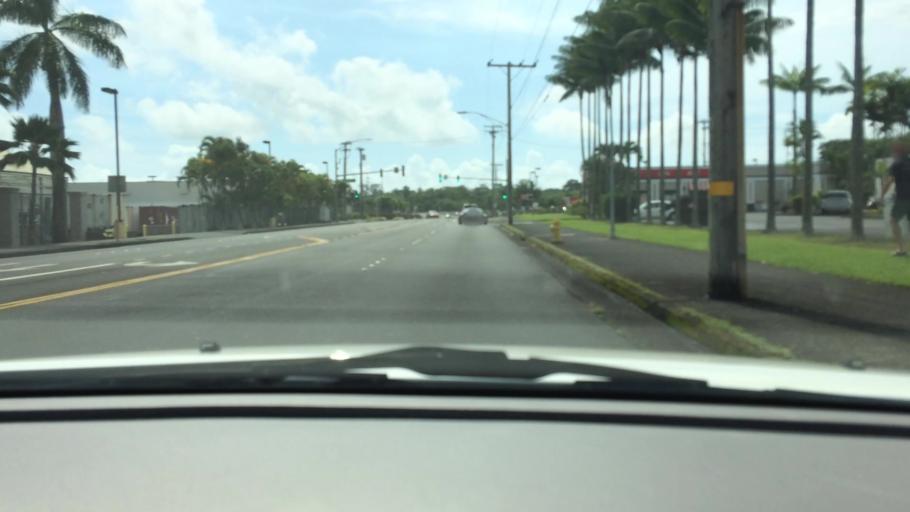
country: US
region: Hawaii
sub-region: Hawaii County
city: Hilo
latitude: 19.6992
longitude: -155.0625
